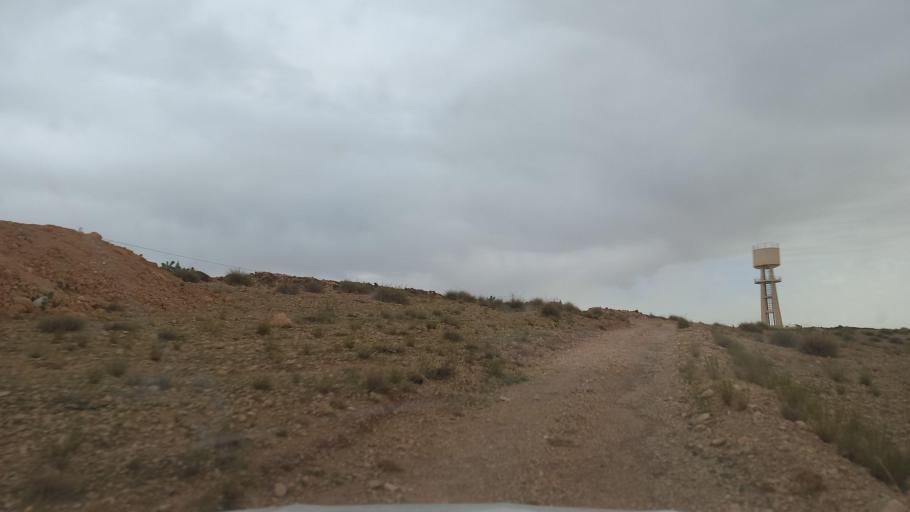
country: TN
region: Al Qasrayn
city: Sbiba
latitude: 35.3840
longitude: 9.0653
